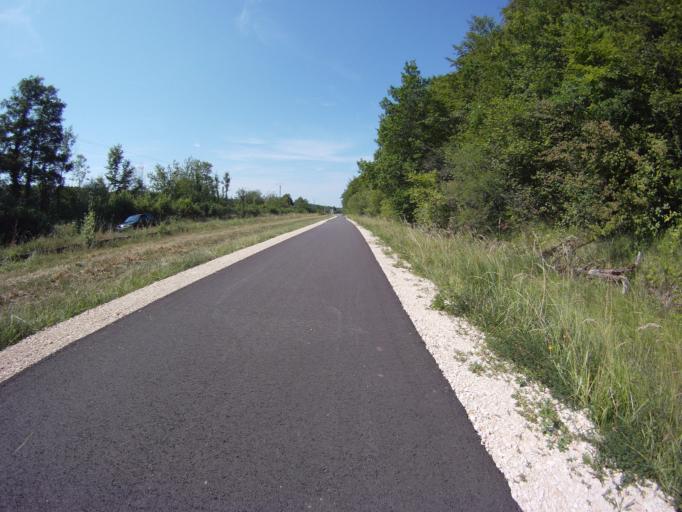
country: FR
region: Lorraine
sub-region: Departement de Meurthe-et-Moselle
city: Villey-Saint-Etienne
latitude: 48.7494
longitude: 6.0083
